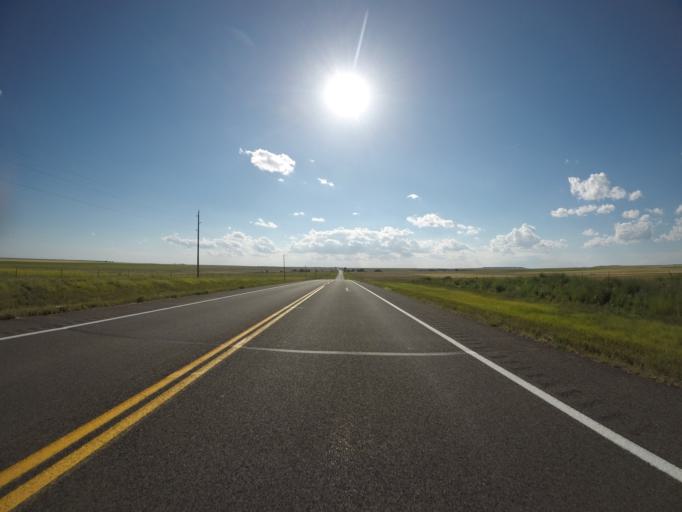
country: US
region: Colorado
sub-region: Morgan County
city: Fort Morgan
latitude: 40.6111
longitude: -103.7834
